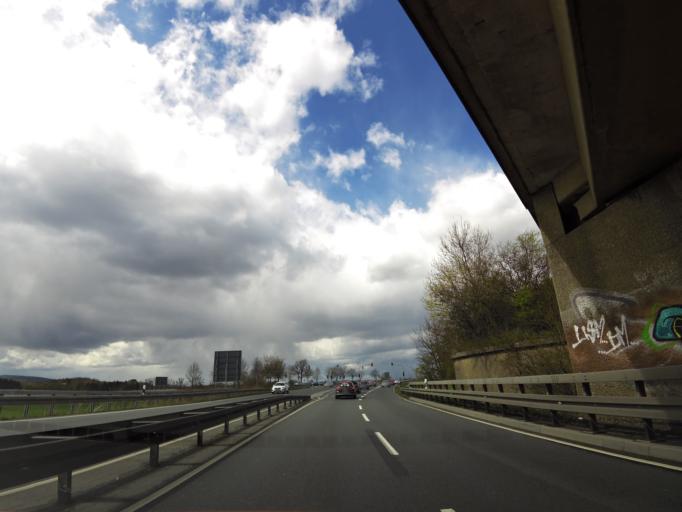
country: DE
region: Lower Saxony
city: Goslar
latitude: 51.9213
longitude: 10.4118
